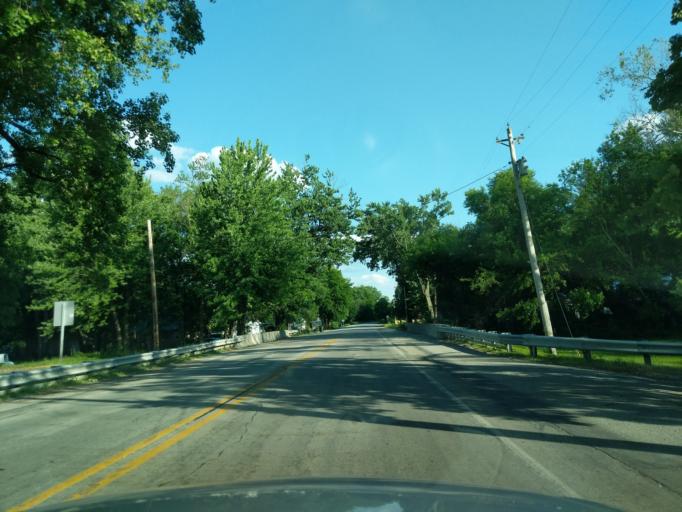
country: US
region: Indiana
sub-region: Whitley County
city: Tri-Lakes
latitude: 41.2743
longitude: -85.4917
